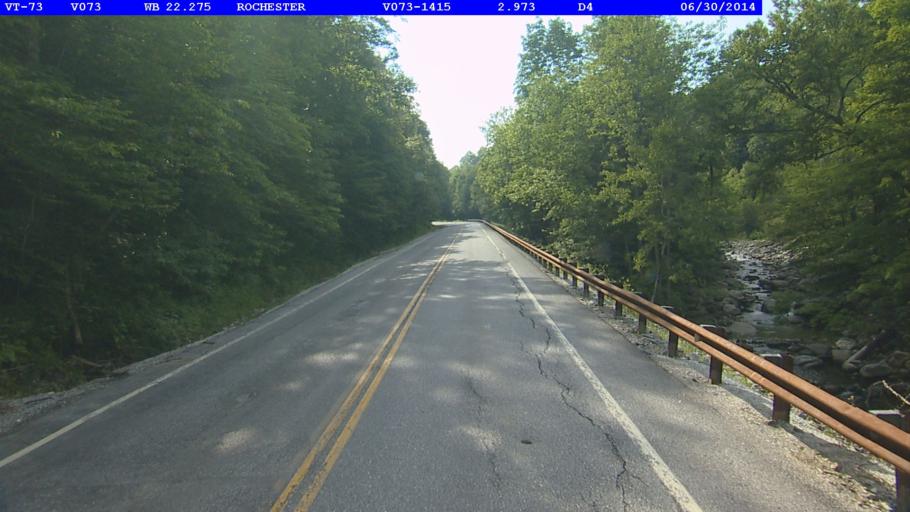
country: US
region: Vermont
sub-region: Rutland County
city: Brandon
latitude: 43.8534
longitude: -72.9114
